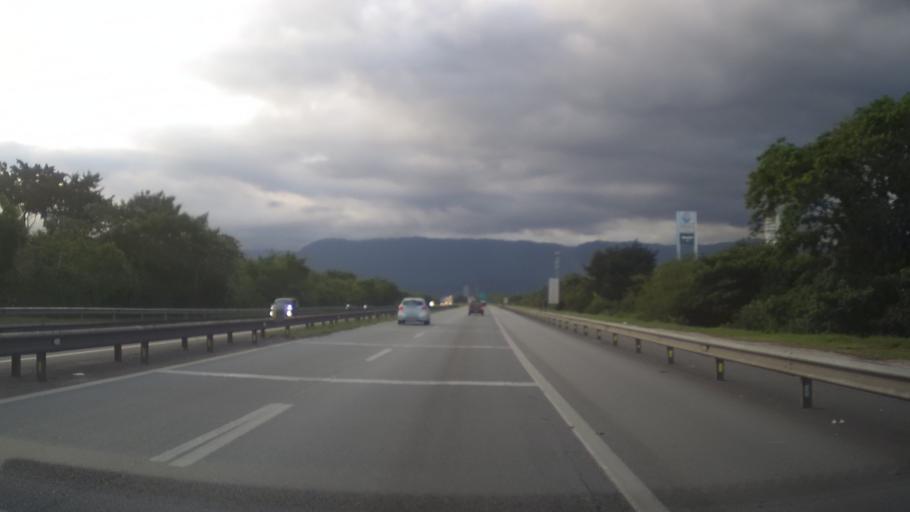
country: BR
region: Sao Paulo
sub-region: Sao Vicente
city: Sao Vicente
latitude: -23.9448
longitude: -46.4176
